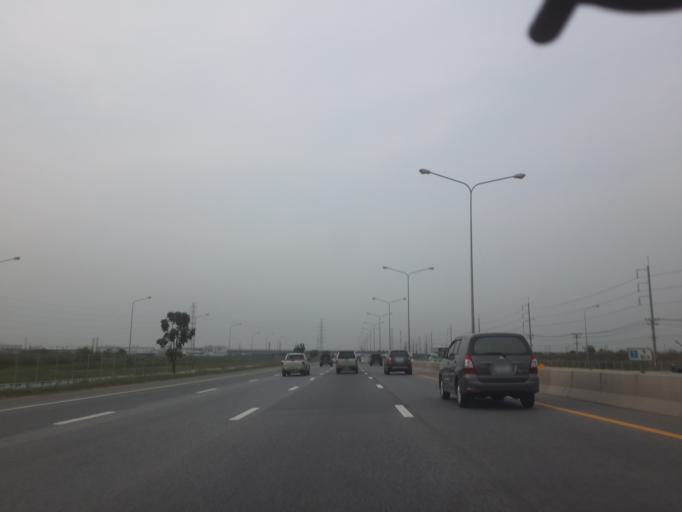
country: TH
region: Chon Buri
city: Phan Thong
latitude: 13.4384
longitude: 101.0461
